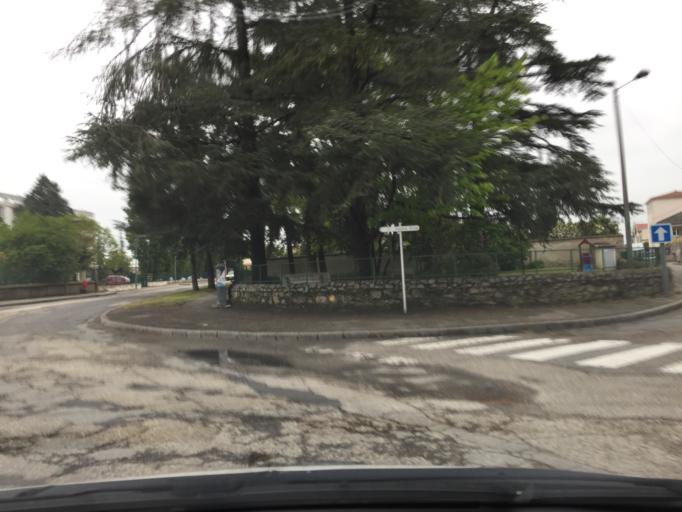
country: FR
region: Rhone-Alpes
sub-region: Departement du Rhone
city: Mornant
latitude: 45.6236
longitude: 4.6684
